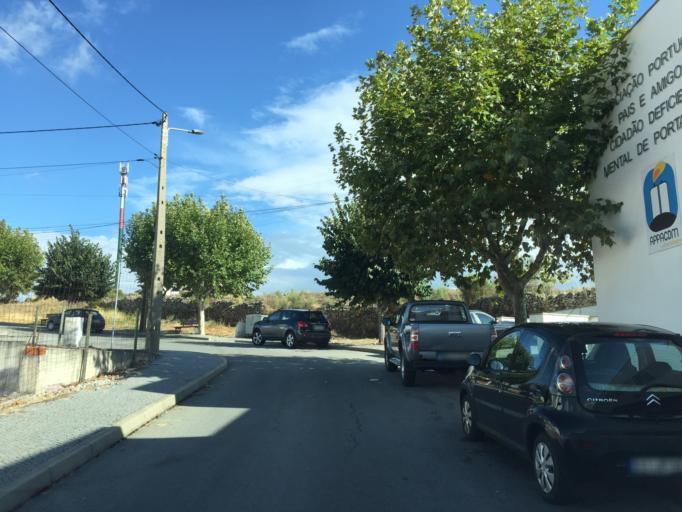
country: PT
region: Portalegre
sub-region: Marvao
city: Marvao
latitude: 39.4106
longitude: -7.3506
